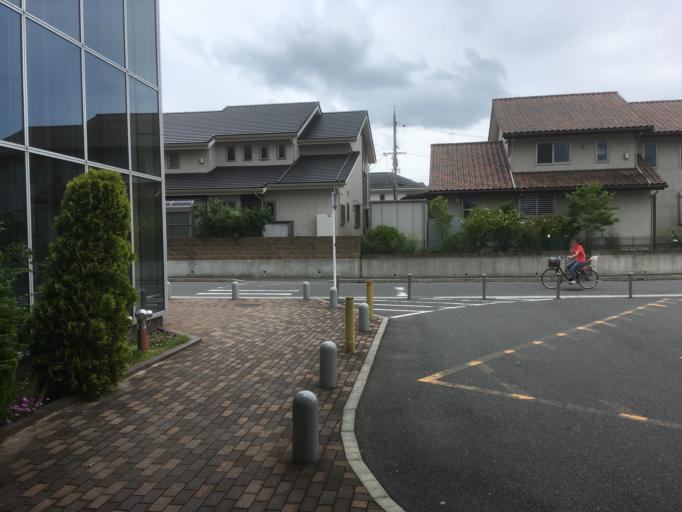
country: JP
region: Nara
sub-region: Ikoma-shi
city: Ikoma
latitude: 34.7208
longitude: 135.7170
